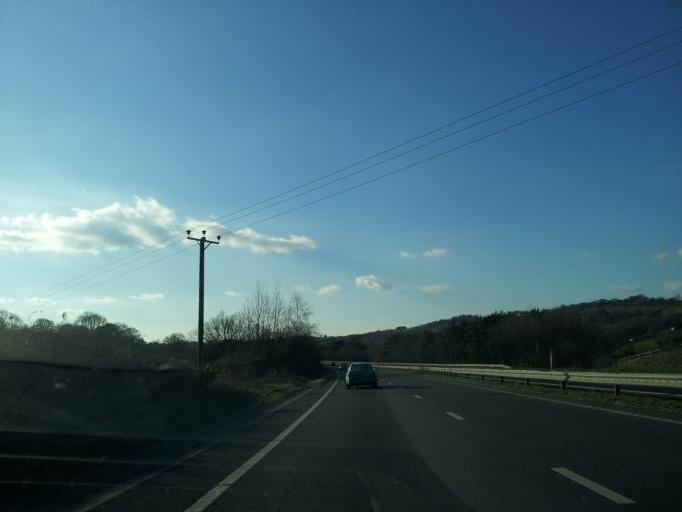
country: GB
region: England
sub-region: Devon
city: Exeter
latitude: 50.7214
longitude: -3.6021
